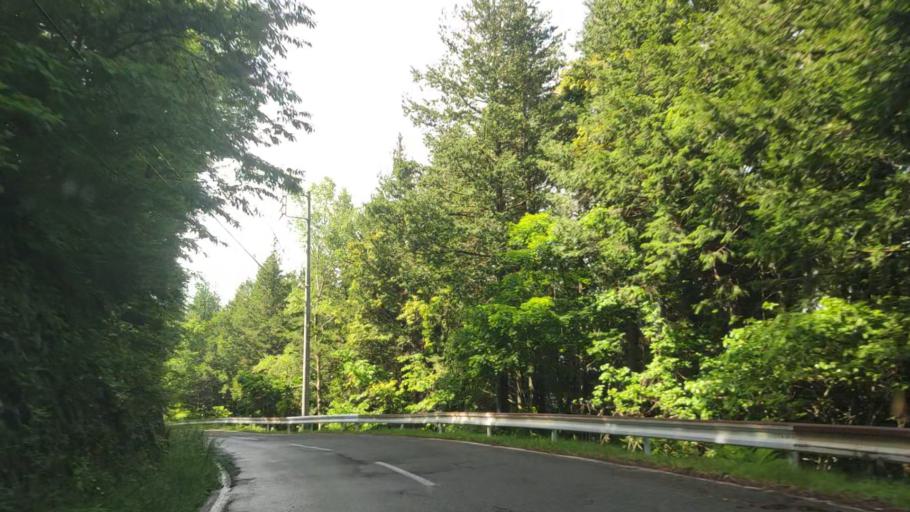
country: JP
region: Nagano
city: Suwa
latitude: 36.0935
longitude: 138.1443
